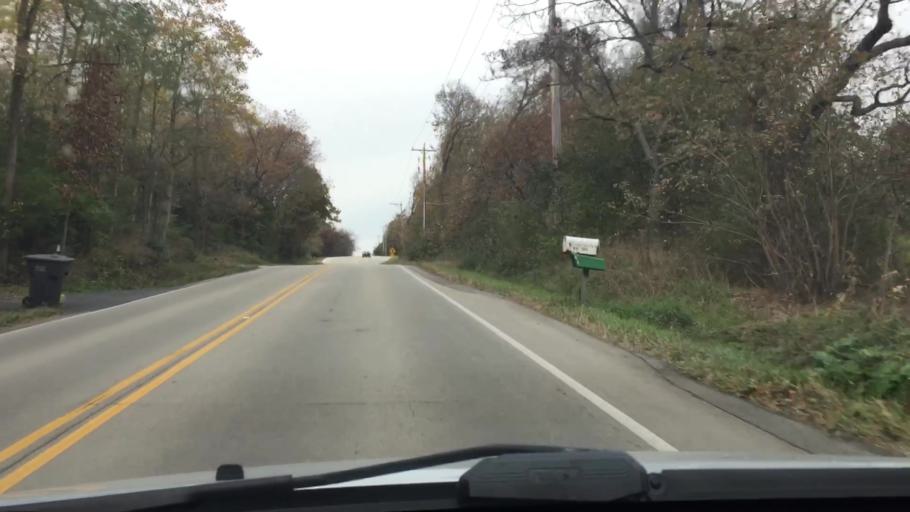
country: US
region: Wisconsin
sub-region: Waukesha County
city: Mukwonago
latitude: 42.8788
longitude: -88.3600
